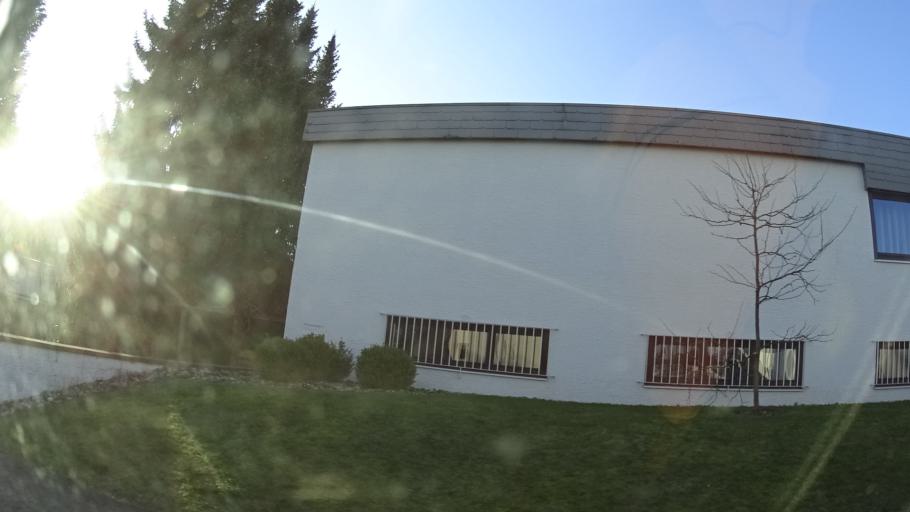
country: DE
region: Saarland
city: Sulzbach
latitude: 49.2677
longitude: 7.0361
